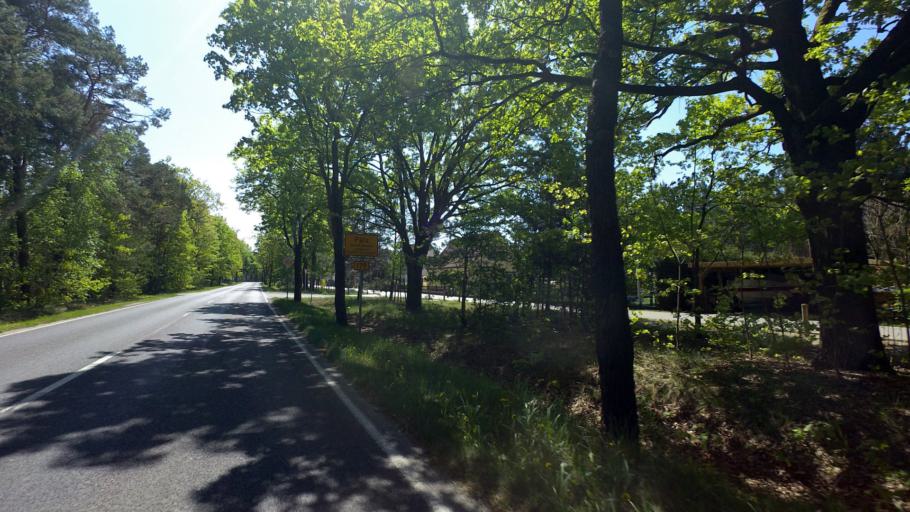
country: DE
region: Brandenburg
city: Bestensee
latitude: 52.2399
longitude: 13.6652
